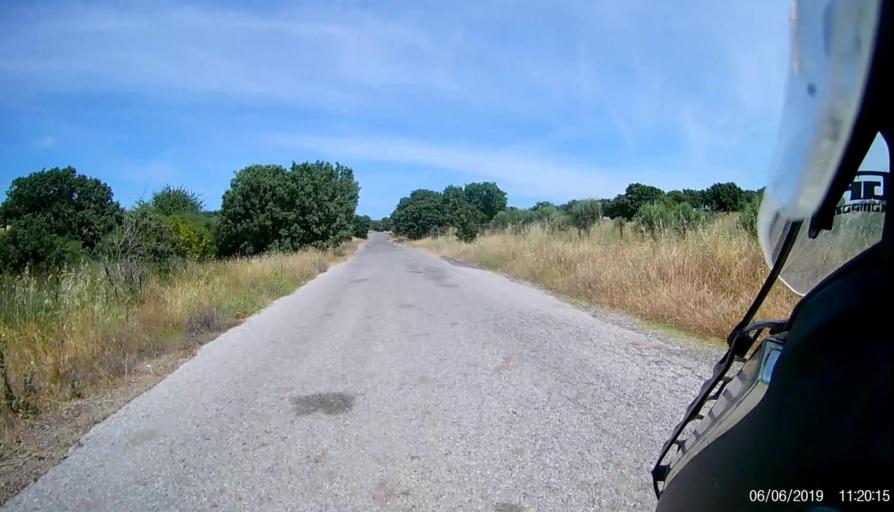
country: TR
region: Canakkale
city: Gulpinar
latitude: 39.6645
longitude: 26.1638
